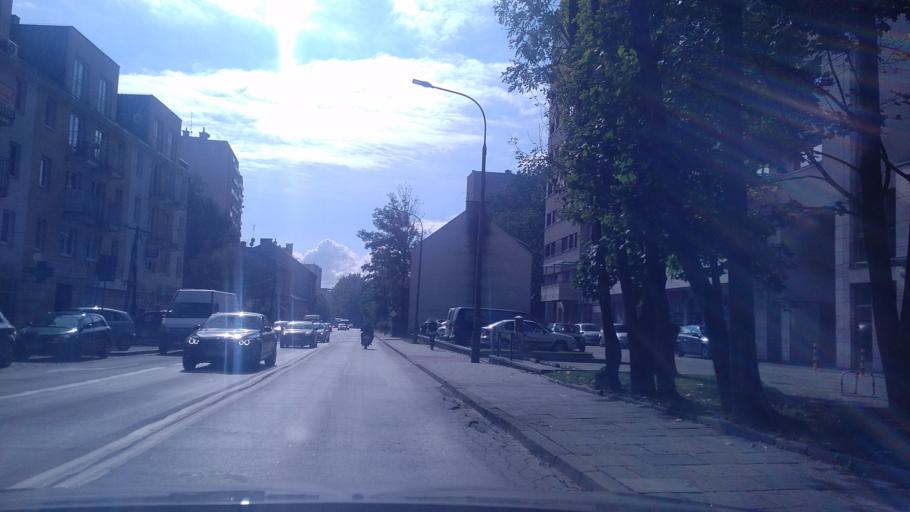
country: PL
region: Lesser Poland Voivodeship
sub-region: Krakow
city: Krakow
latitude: 50.0802
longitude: 19.9188
